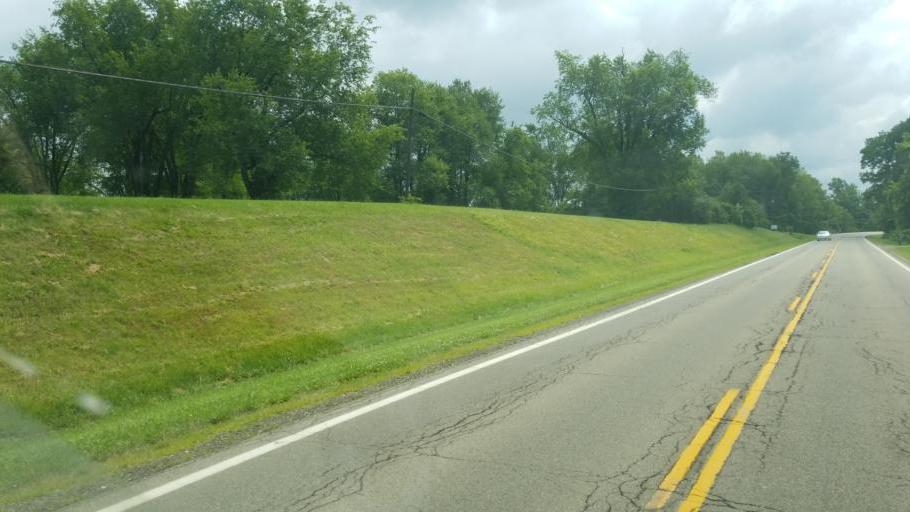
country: US
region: Ohio
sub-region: Richland County
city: Lexington
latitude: 40.6972
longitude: -82.6176
